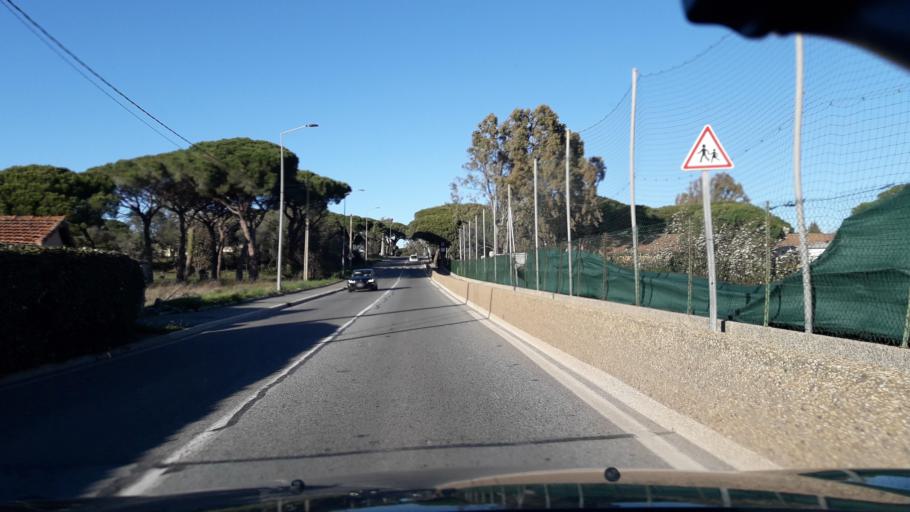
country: FR
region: Provence-Alpes-Cote d'Azur
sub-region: Departement du Var
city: Frejus
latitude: 43.4543
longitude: 6.7270
